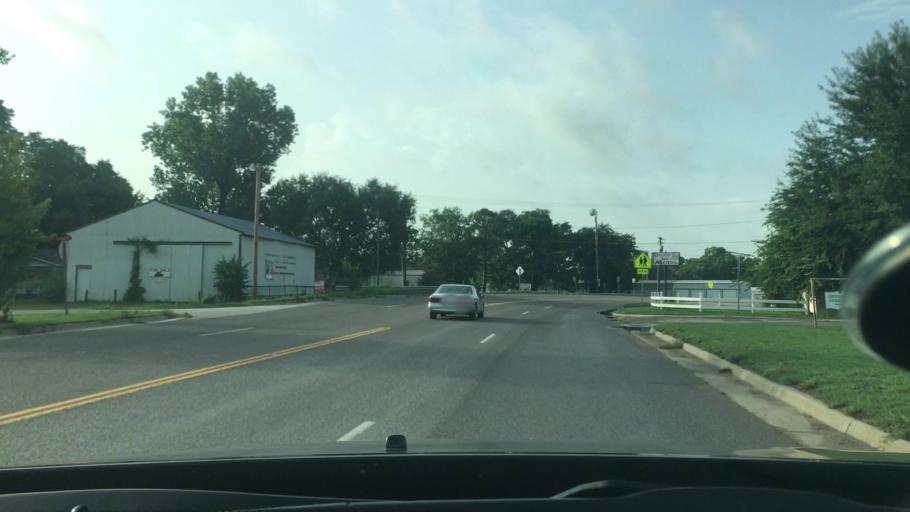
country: US
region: Oklahoma
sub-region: Murray County
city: Davis
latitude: 34.5007
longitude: -97.1257
